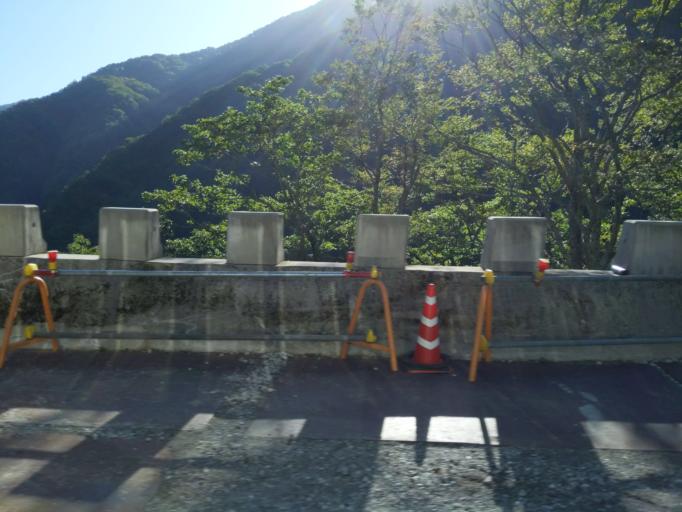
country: JP
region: Toyama
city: Kamiichi
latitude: 36.5081
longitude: 137.4486
